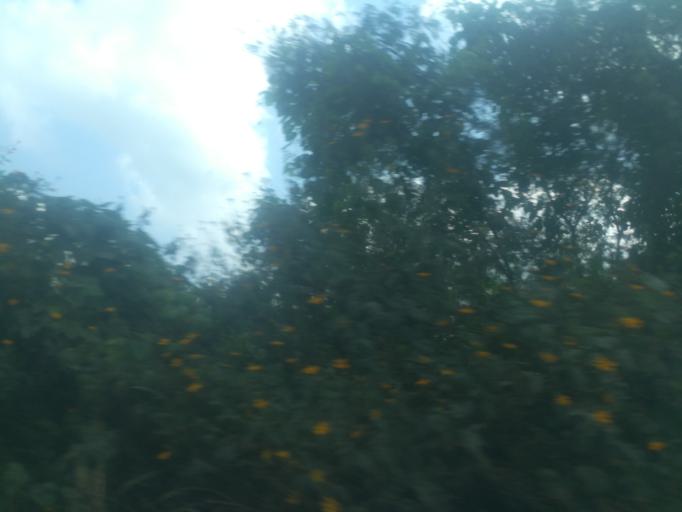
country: NG
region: Oyo
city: Moniya
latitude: 7.5863
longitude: 3.9150
